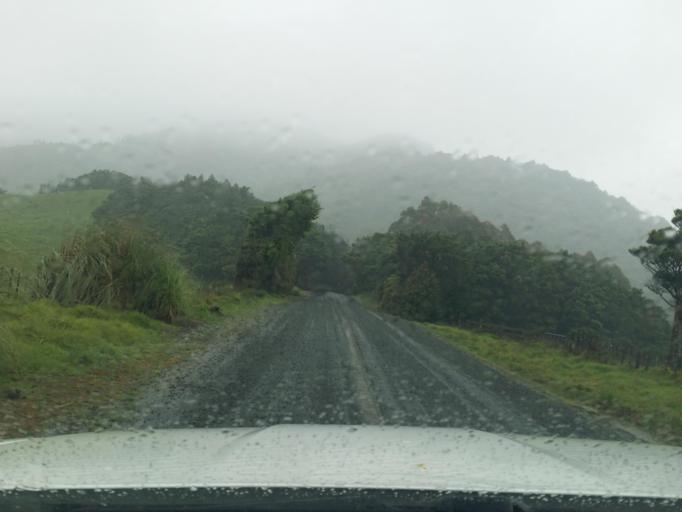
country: NZ
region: Northland
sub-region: Kaipara District
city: Dargaville
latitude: -35.7577
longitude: 173.9602
